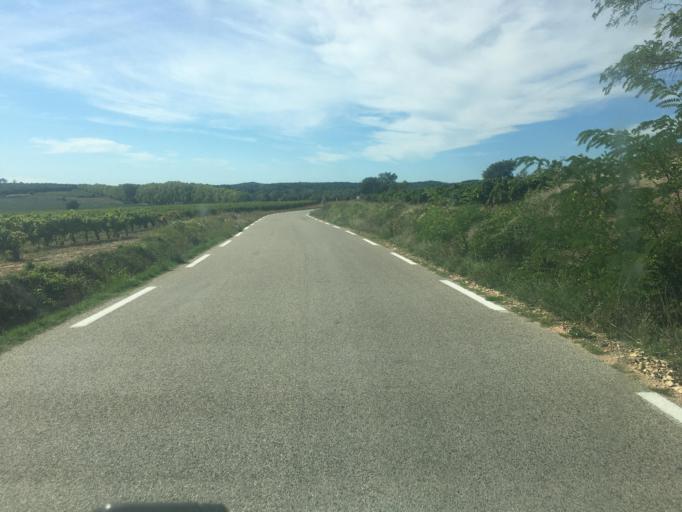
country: FR
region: Languedoc-Roussillon
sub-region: Departement du Gard
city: Connaux
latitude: 44.0437
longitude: 4.5618
